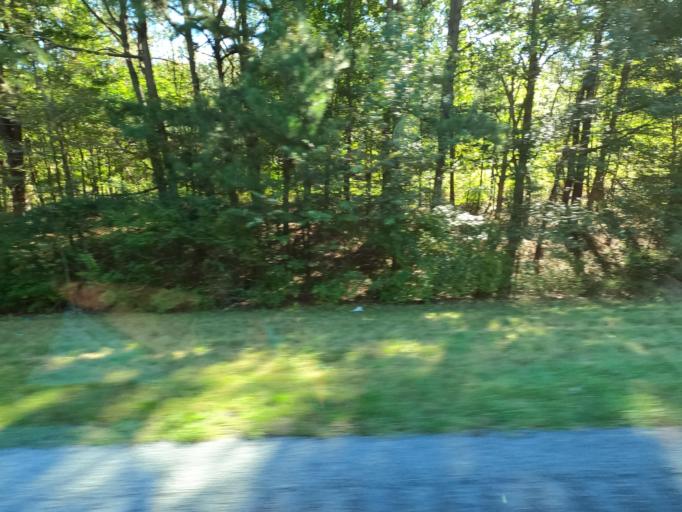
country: US
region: Tennessee
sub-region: Cheatham County
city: Kingston Springs
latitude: 36.0485
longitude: -87.1436
